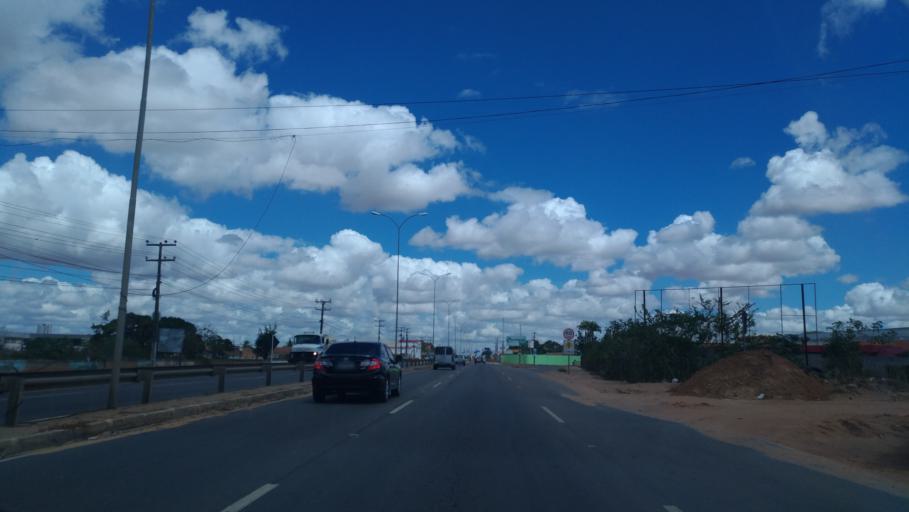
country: BR
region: Alagoas
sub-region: Arapiraca
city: Arapiraca
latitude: -9.7347
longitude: -36.6506
